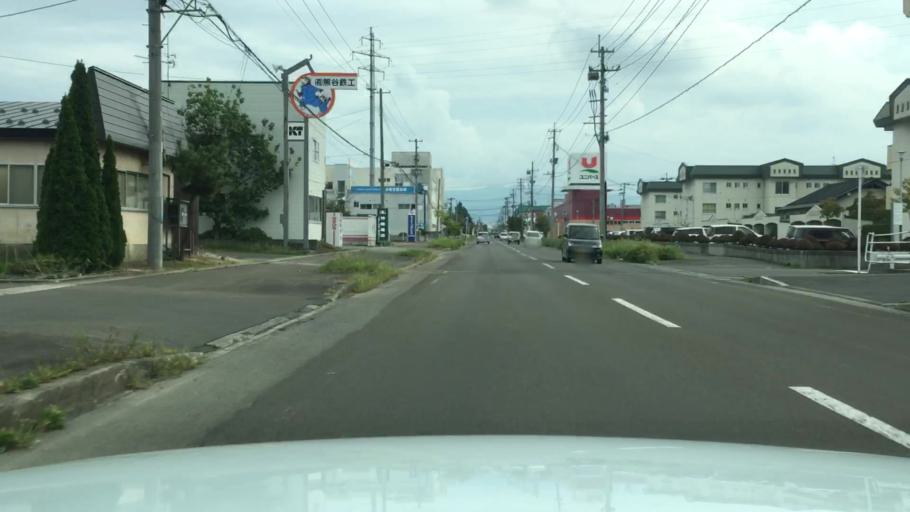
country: JP
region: Aomori
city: Hirosaki
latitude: 40.6241
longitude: 140.4852
